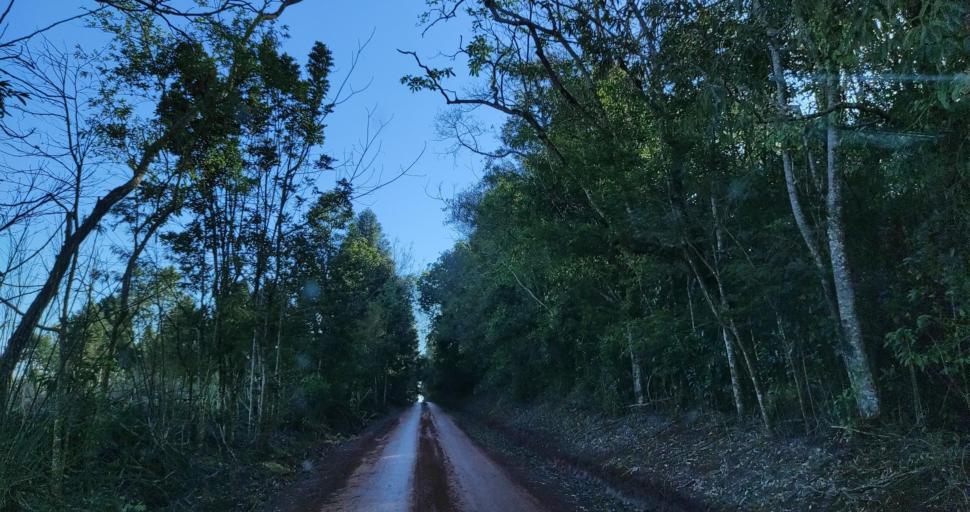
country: AR
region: Misiones
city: Capiovi
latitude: -26.8782
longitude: -55.0165
